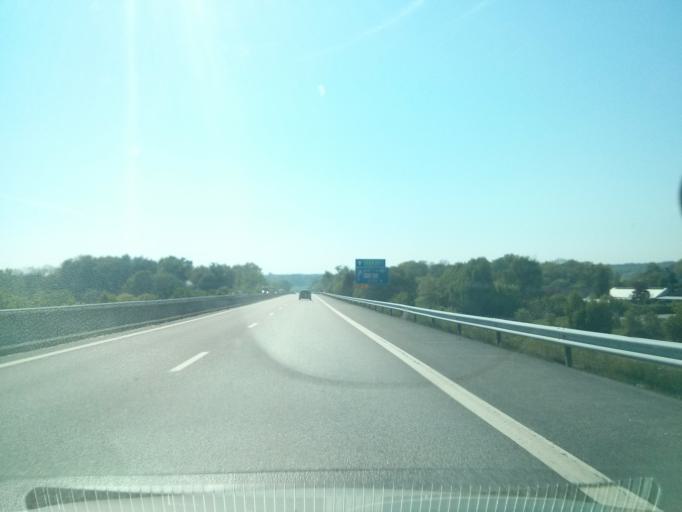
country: SE
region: Blekinge
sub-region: Karlskrona Kommun
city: Nattraby
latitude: 56.2096
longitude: 15.5448
